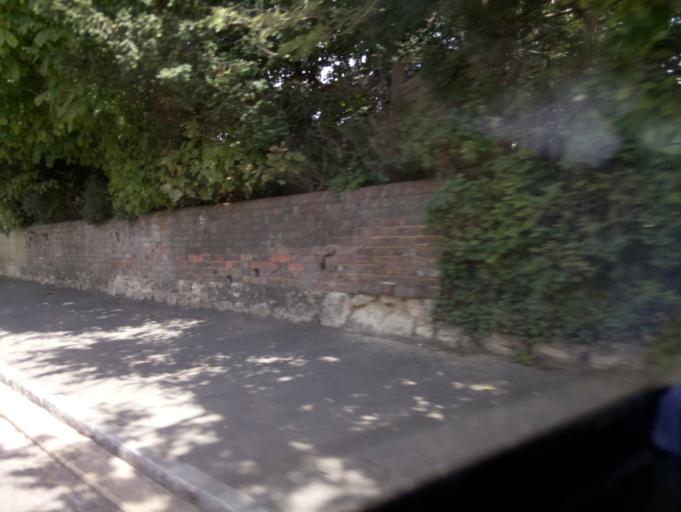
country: GB
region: England
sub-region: Buckinghamshire
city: Aylesbury
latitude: 51.8778
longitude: -0.8340
